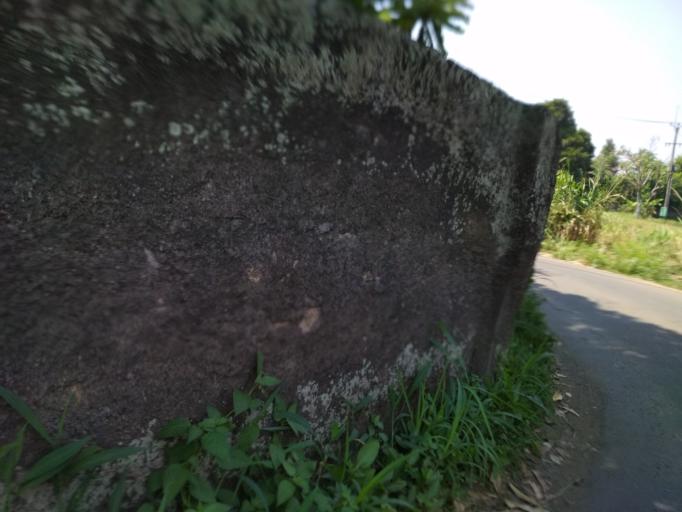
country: ID
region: West Java
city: Ciampea
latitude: -6.5639
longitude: 106.7450
